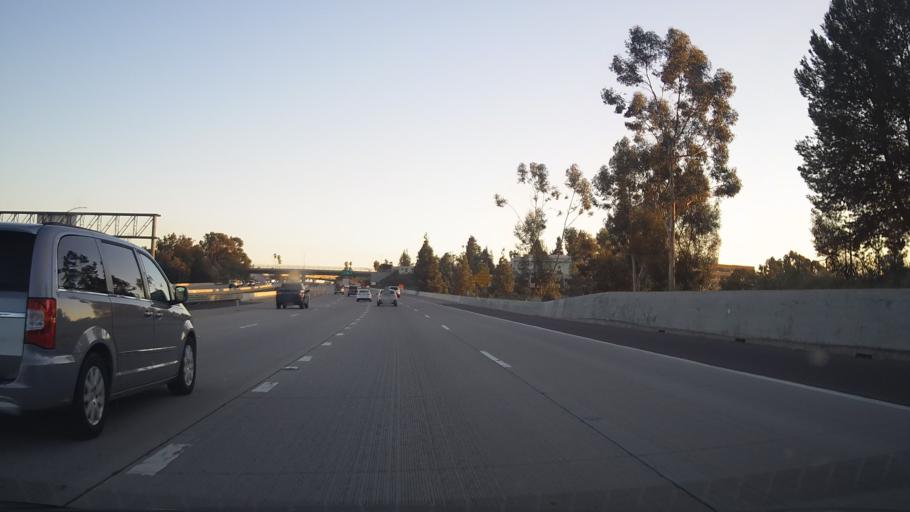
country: US
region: California
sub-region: San Diego County
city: La Mesa
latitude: 32.7861
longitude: -117.0065
